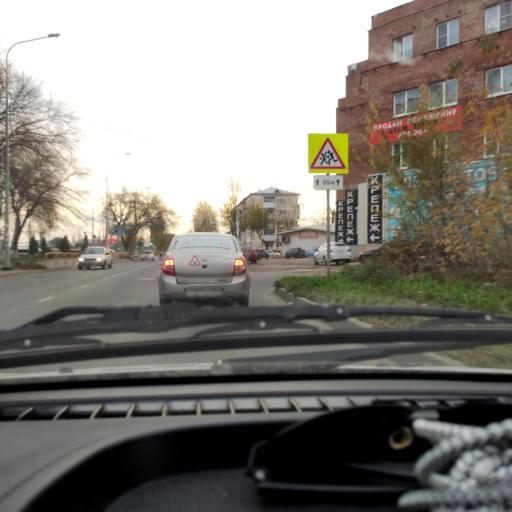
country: RU
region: Samara
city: Tol'yatti
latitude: 53.5374
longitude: 49.4082
